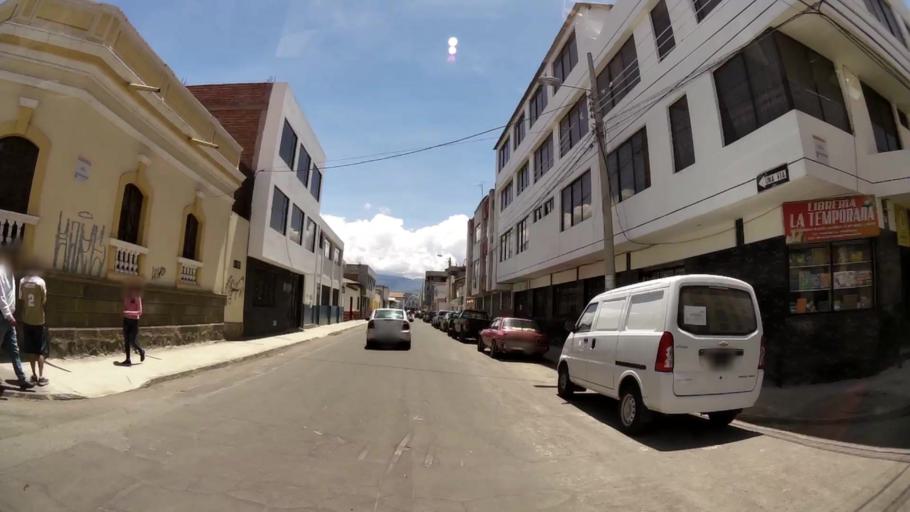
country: EC
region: Chimborazo
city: Riobamba
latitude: -1.6742
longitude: -78.6528
